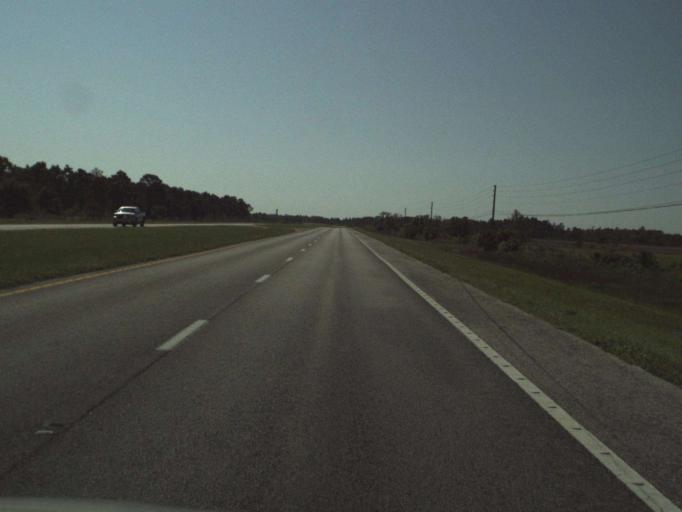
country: US
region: Florida
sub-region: Orange County
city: Wedgefield
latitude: 28.4854
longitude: -81.0340
